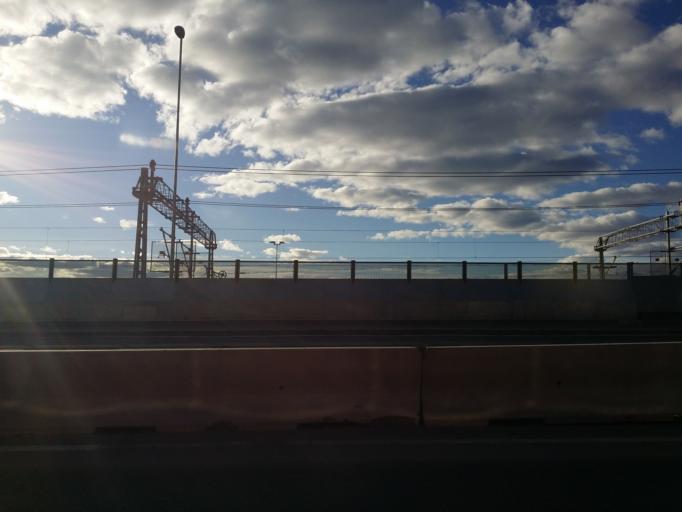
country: NO
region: Oslo
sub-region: Oslo
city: Oslo
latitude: 59.8984
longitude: 10.7561
